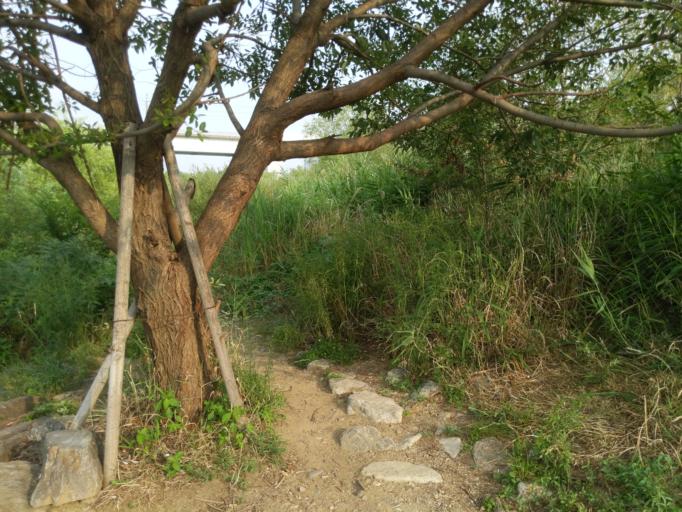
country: KR
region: Gyeonggi-do
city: Kwangmyong
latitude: 37.5385
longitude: 126.9038
